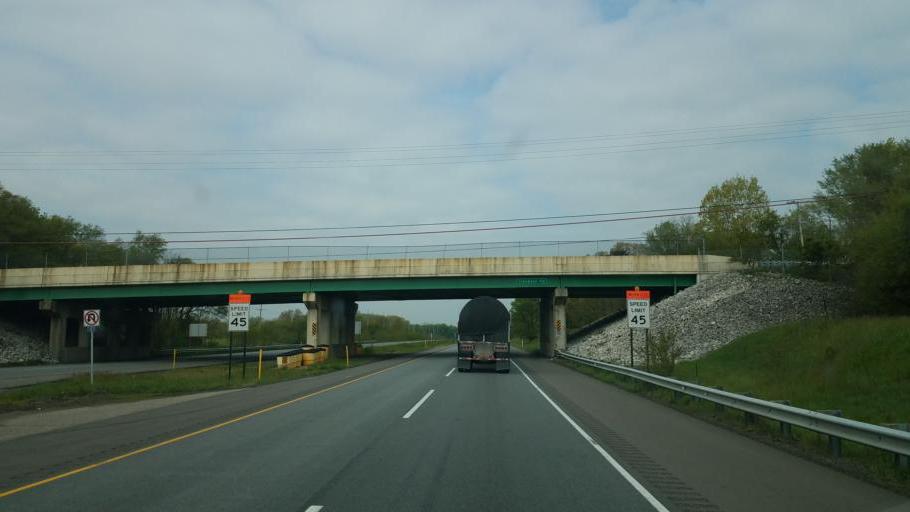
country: US
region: Indiana
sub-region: Saint Joseph County
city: Georgetown
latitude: 41.7158
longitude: -86.2154
